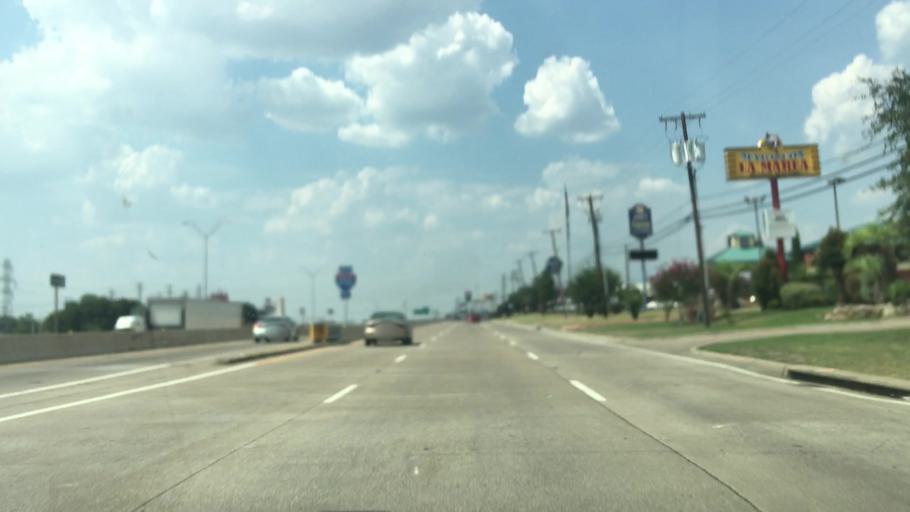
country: US
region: Texas
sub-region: Dallas County
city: DeSoto
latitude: 32.5990
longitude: -96.8222
